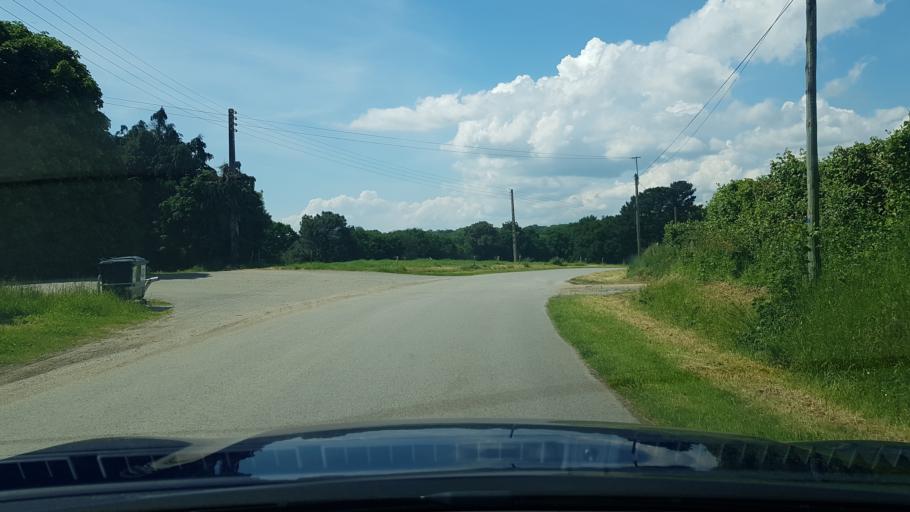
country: FR
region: Brittany
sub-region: Departement du Finistere
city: Clohars-Carnoet
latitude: 47.7880
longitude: -3.5584
